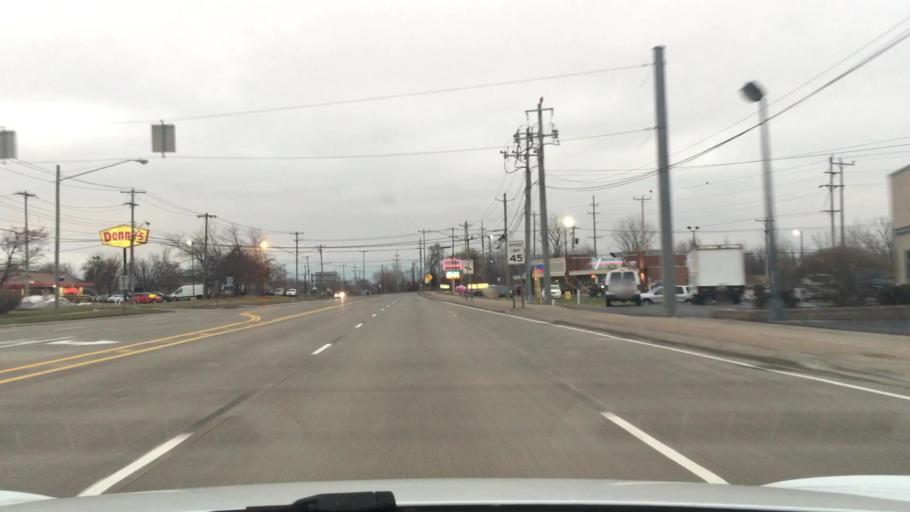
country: US
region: New York
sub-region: Erie County
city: Williamsville
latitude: 42.9344
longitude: -78.7166
